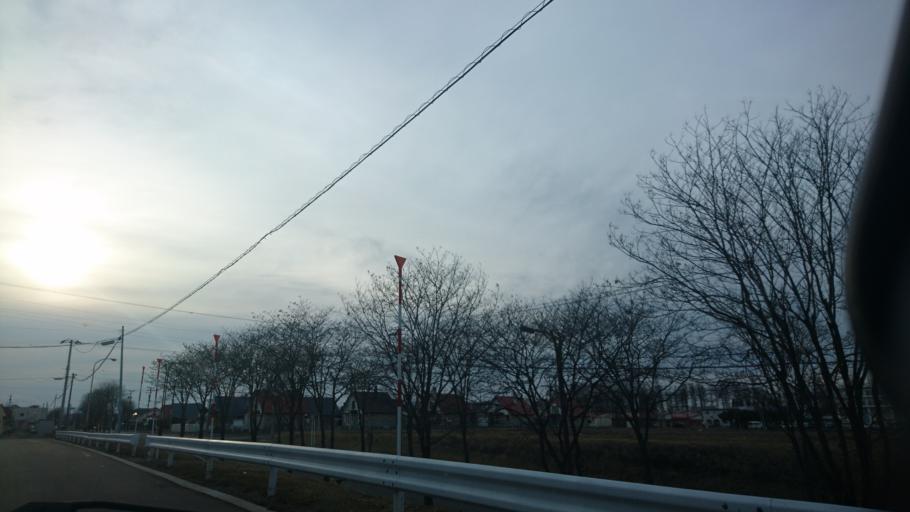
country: JP
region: Hokkaido
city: Otofuke
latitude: 43.0015
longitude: 143.1940
